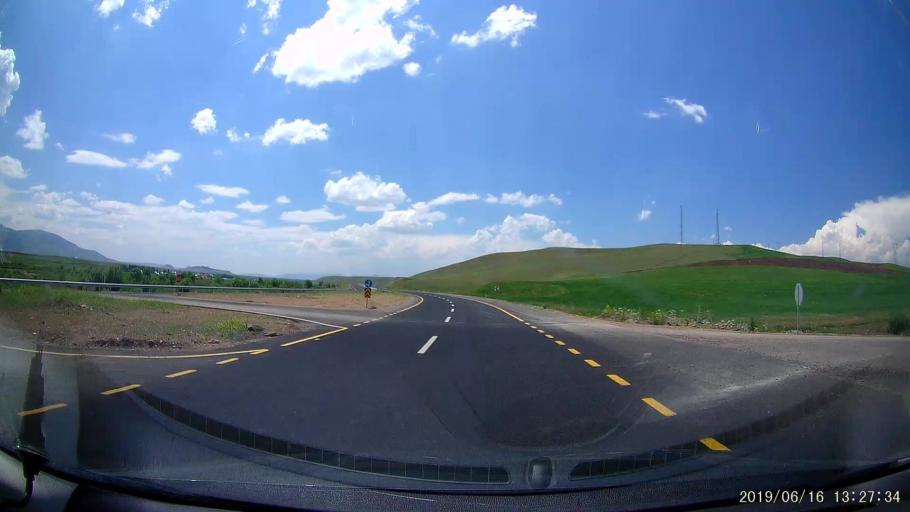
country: TR
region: Agri
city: Murat
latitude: 39.6717
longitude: 43.3076
